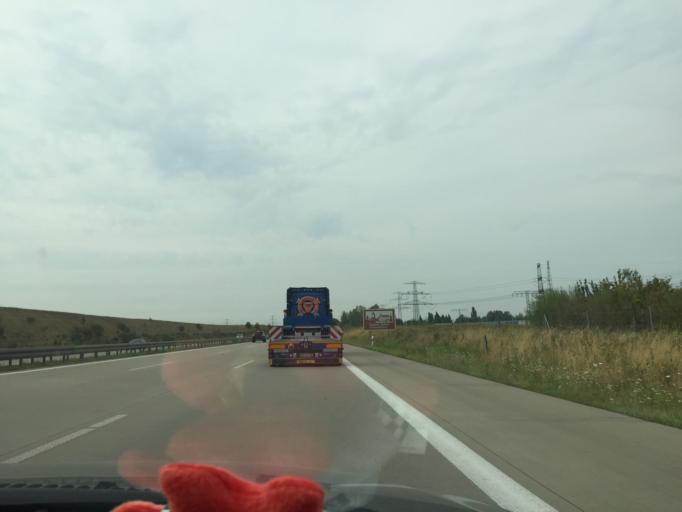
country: DE
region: Brandenburg
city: Neuenhagen
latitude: 52.5307
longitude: 13.7087
